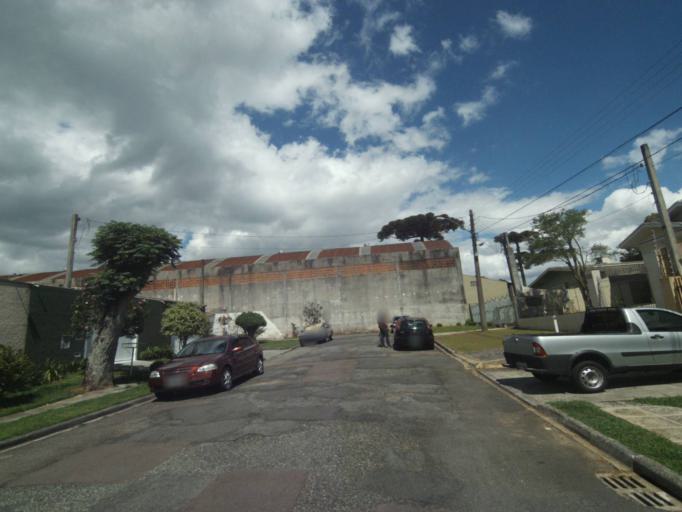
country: BR
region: Parana
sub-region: Curitiba
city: Curitiba
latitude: -25.4318
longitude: -49.3326
